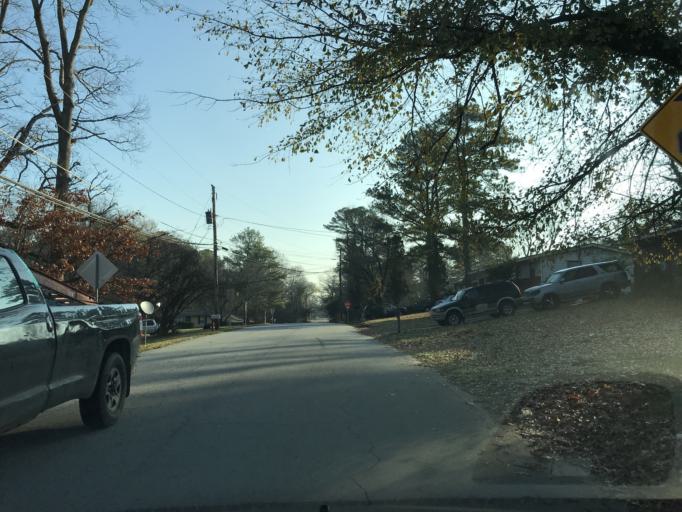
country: US
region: Georgia
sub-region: Fulton County
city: College Park
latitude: 33.6146
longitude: -84.4365
